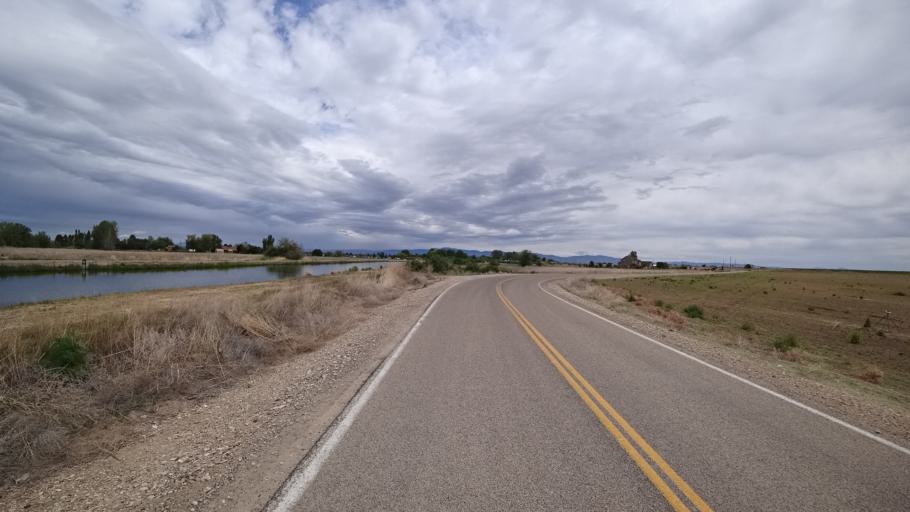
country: US
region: Idaho
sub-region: Ada County
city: Kuna
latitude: 43.4698
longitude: -116.4425
